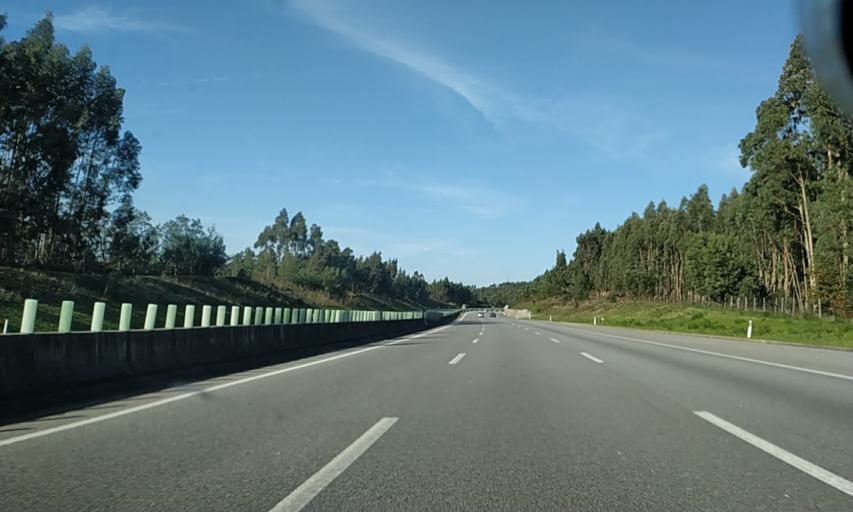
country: PT
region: Coimbra
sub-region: Condeixa-A-Nova
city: Condeixa-a-Nova
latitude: 40.1499
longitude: -8.4929
